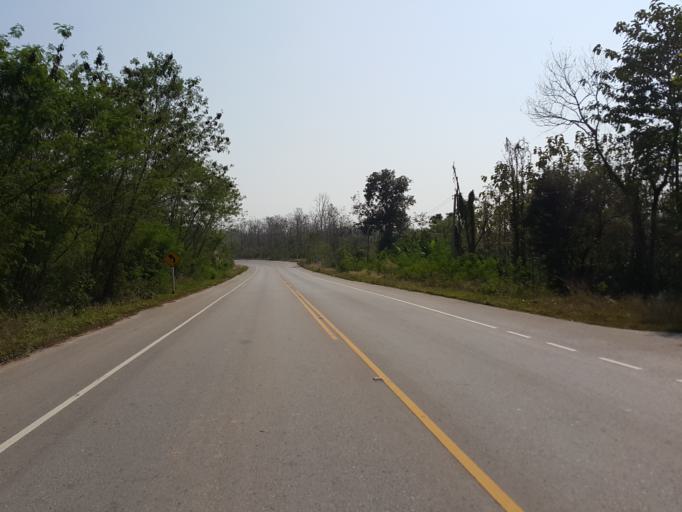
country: TH
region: Lampang
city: Mueang Pan
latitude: 18.8474
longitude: 99.6012
